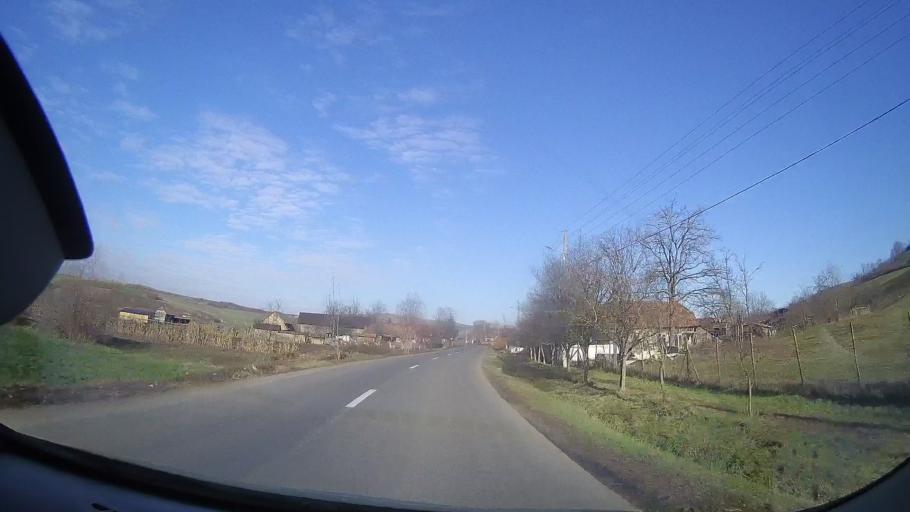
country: RO
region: Mures
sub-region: Comuna Band
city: Band
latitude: 46.5566
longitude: 24.3352
